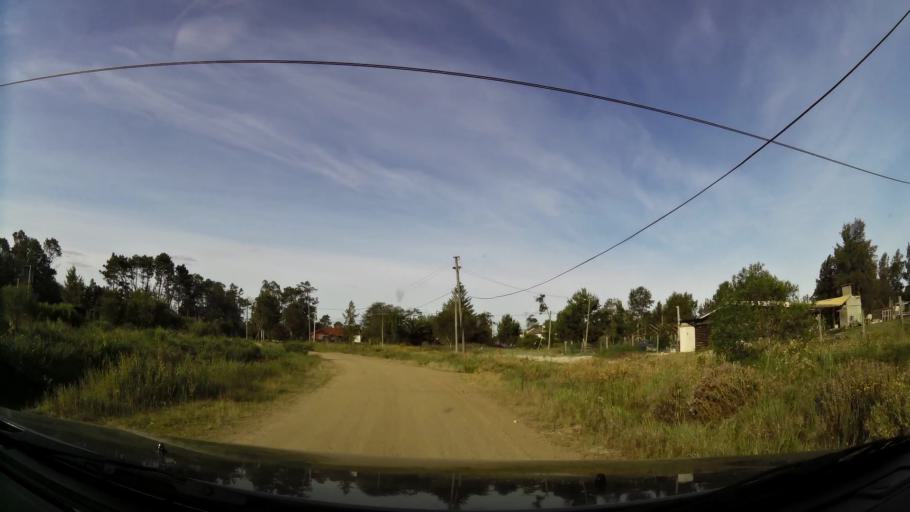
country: UY
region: Canelones
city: Empalme Olmos
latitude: -34.7900
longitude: -55.8575
